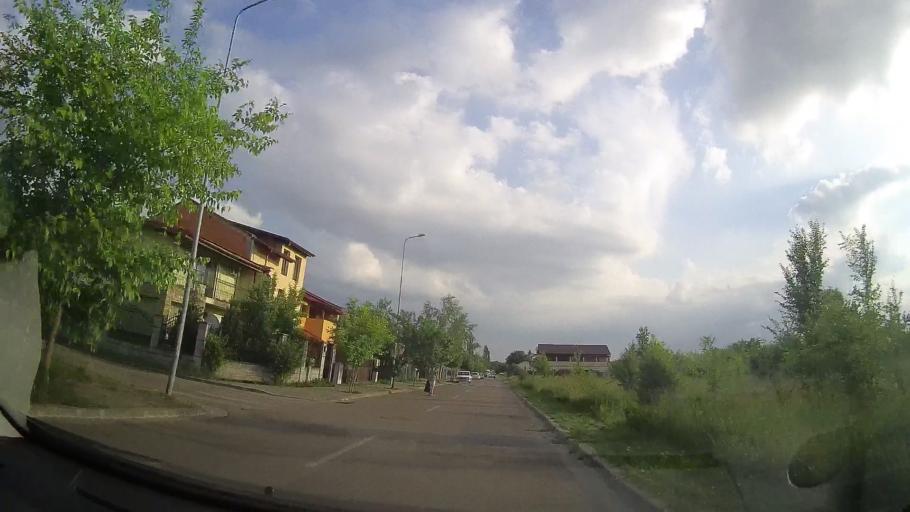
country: RO
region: Timis
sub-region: Comuna Dumbravita
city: Dumbravita
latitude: 45.7845
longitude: 21.2329
